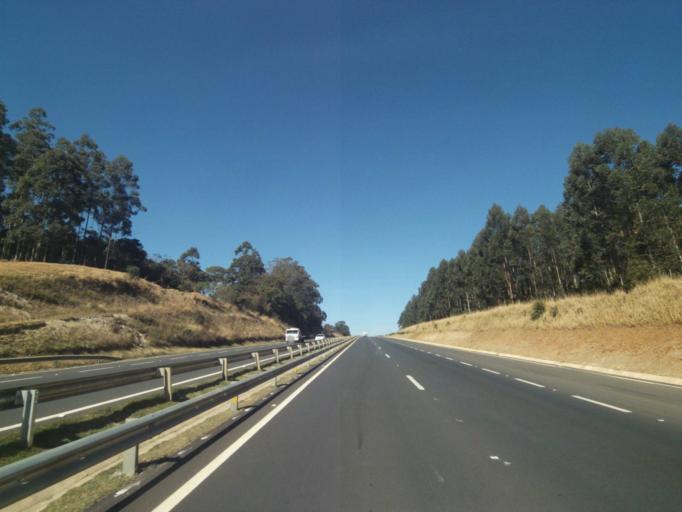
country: BR
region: Parana
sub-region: Tibagi
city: Tibagi
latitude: -24.8401
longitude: -50.4757
